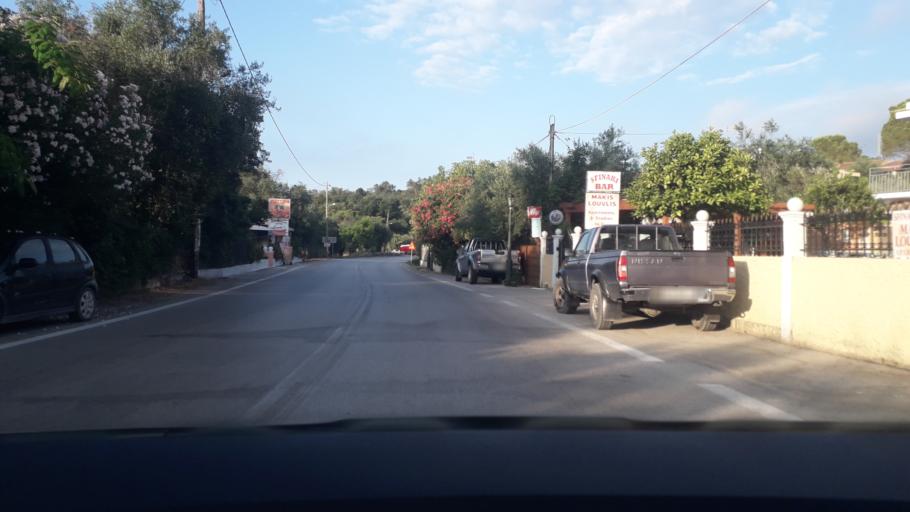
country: GR
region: Ionian Islands
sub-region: Nomos Kerkyras
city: Agios Matthaios
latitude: 39.4780
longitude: 19.9257
